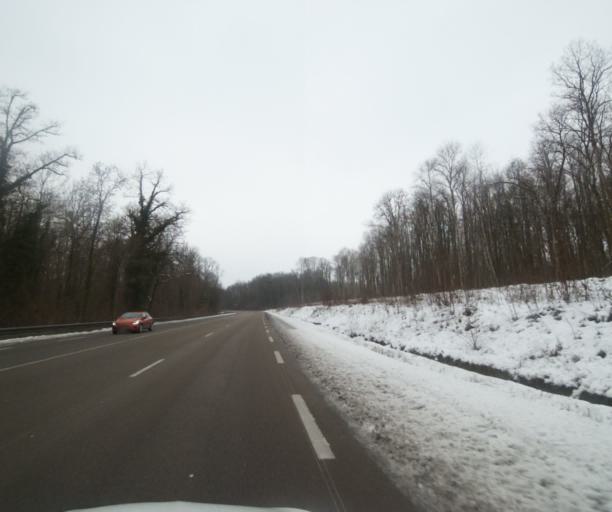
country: FR
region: Champagne-Ardenne
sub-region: Departement de la Haute-Marne
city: Saint-Dizier
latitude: 48.6121
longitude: 4.9171
